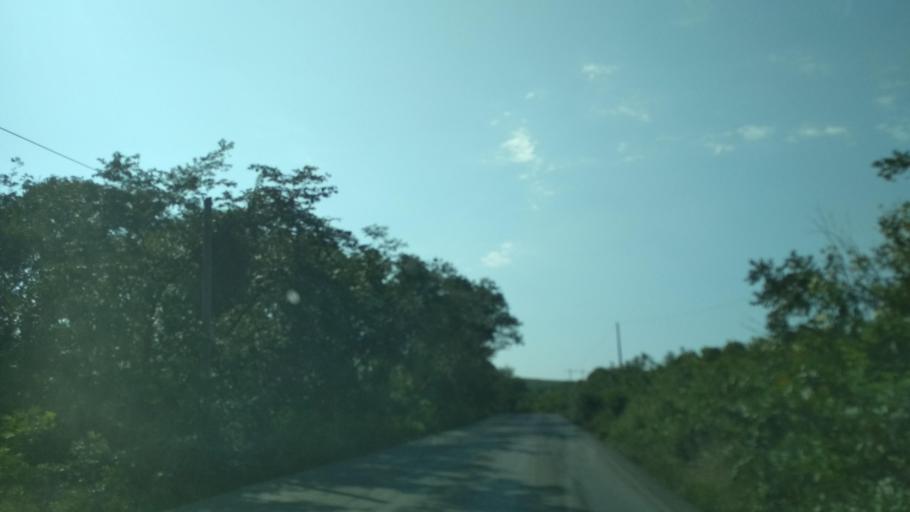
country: MM
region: Shan
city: Taunggyi
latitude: 20.3843
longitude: 97.2895
